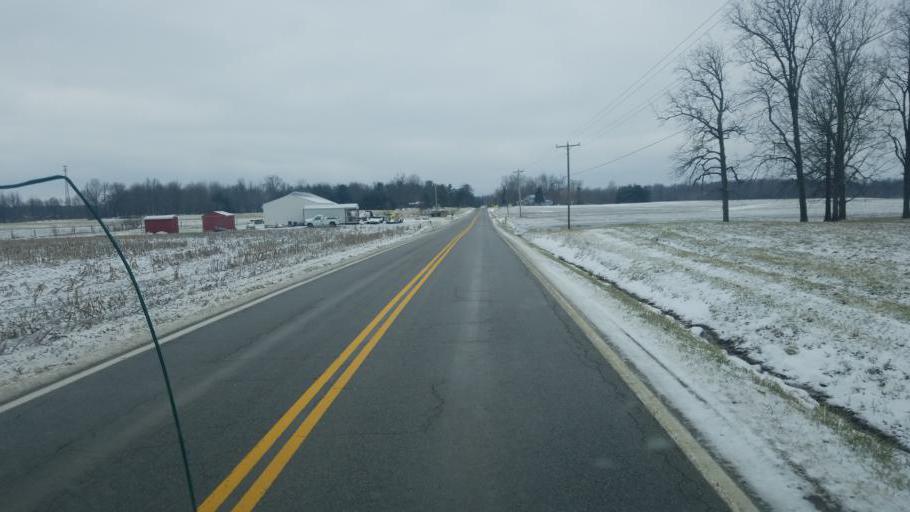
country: US
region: Ohio
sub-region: Licking County
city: Johnstown
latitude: 40.1104
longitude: -82.7039
